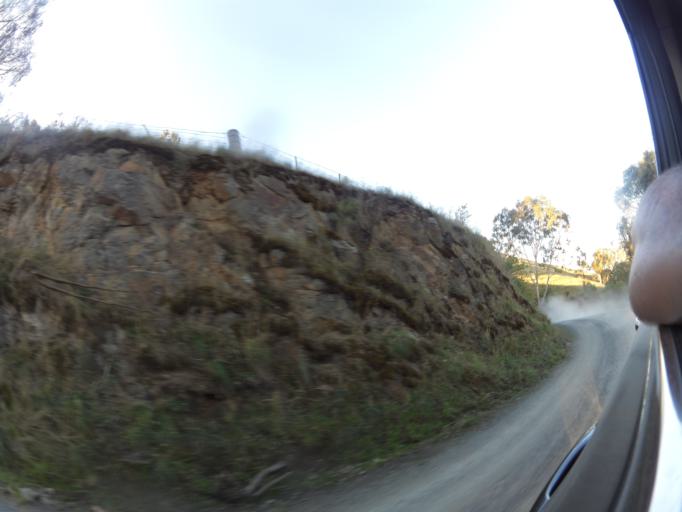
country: AU
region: Victoria
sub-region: Murrindindi
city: Alexandra
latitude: -37.1530
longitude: 145.5276
